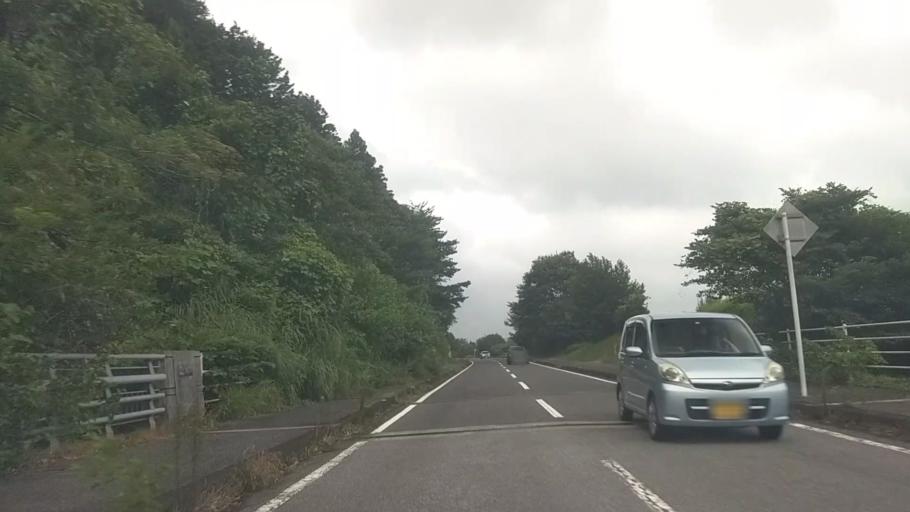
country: JP
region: Chiba
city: Kawaguchi
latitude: 35.2422
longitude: 140.0831
